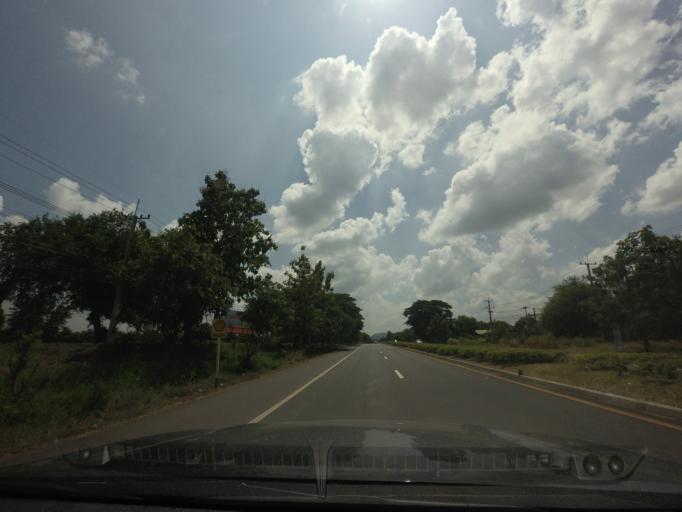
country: TH
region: Phetchabun
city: Phetchabun
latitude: 16.2780
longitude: 101.0601
